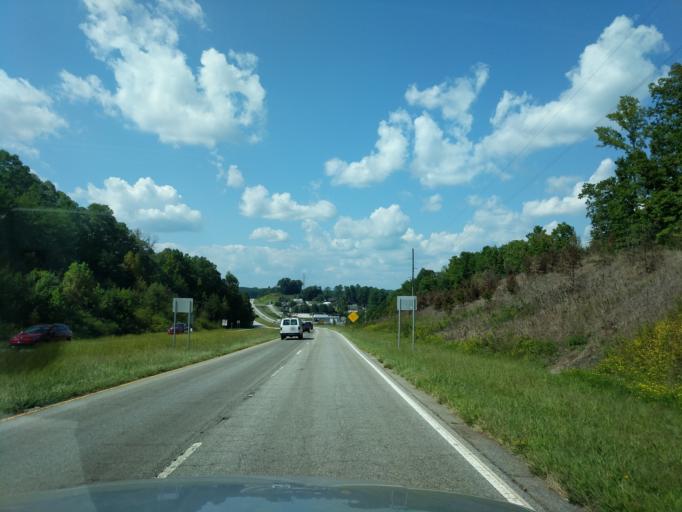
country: US
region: South Carolina
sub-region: Anderson County
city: Powdersville
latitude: 34.8178
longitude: -82.5193
